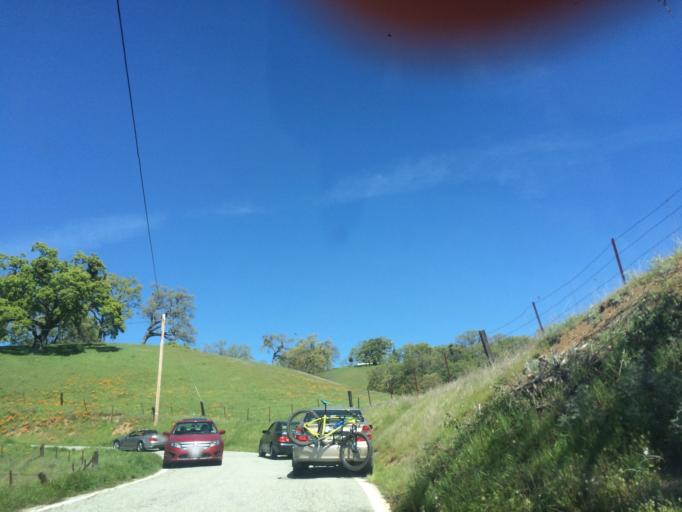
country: US
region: California
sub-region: Santa Clara County
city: Morgan Hill
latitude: 37.1834
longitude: -121.5575
